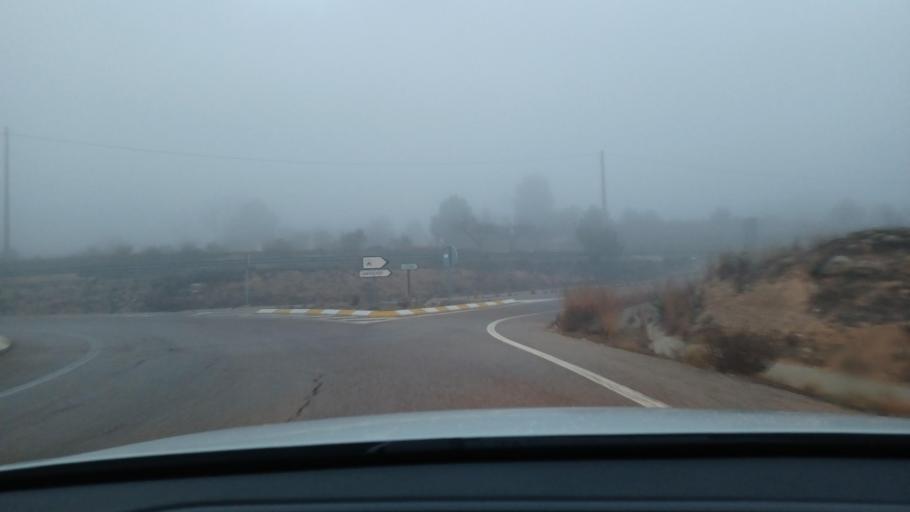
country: ES
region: Valencia
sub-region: Provincia de Valencia
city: La Font de la Figuera
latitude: 38.8342
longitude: -0.8758
